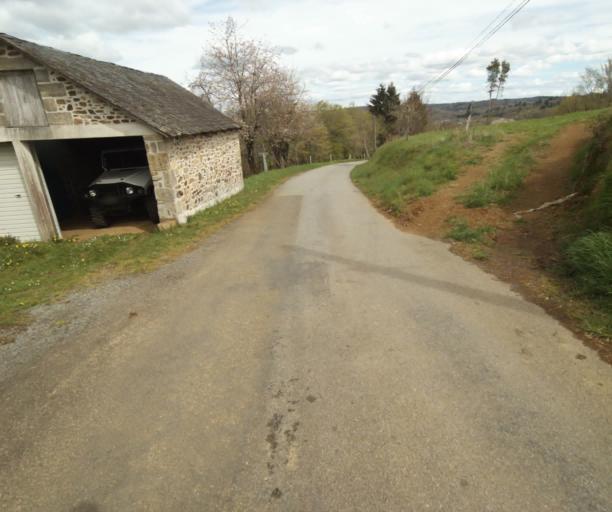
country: FR
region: Limousin
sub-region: Departement de la Correze
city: Laguenne
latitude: 45.2246
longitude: 1.8474
